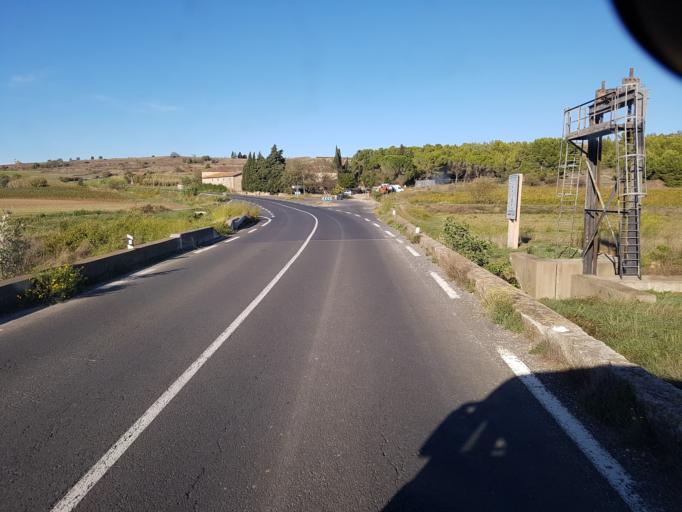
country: FR
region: Languedoc-Roussillon
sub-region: Departement de l'Aude
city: Coursan
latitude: 43.2657
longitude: 3.0807
